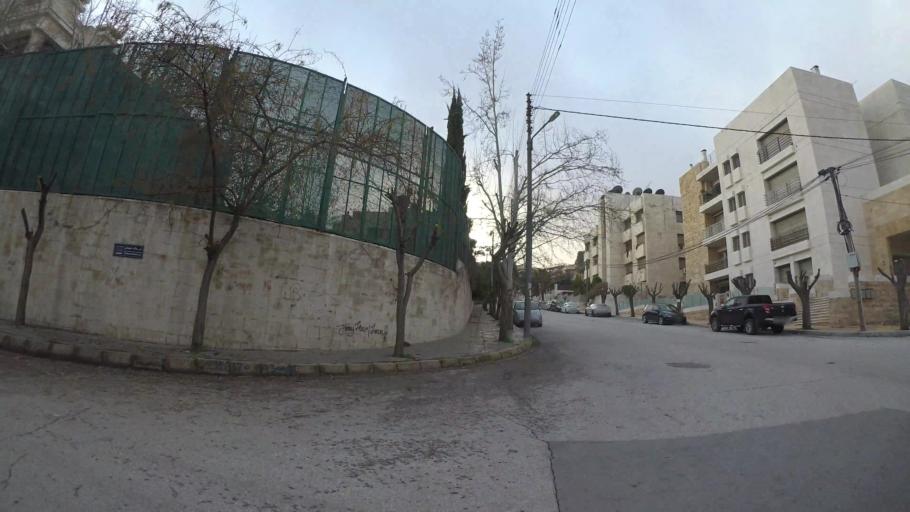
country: JO
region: Amman
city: Amman
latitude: 31.9633
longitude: 35.8860
